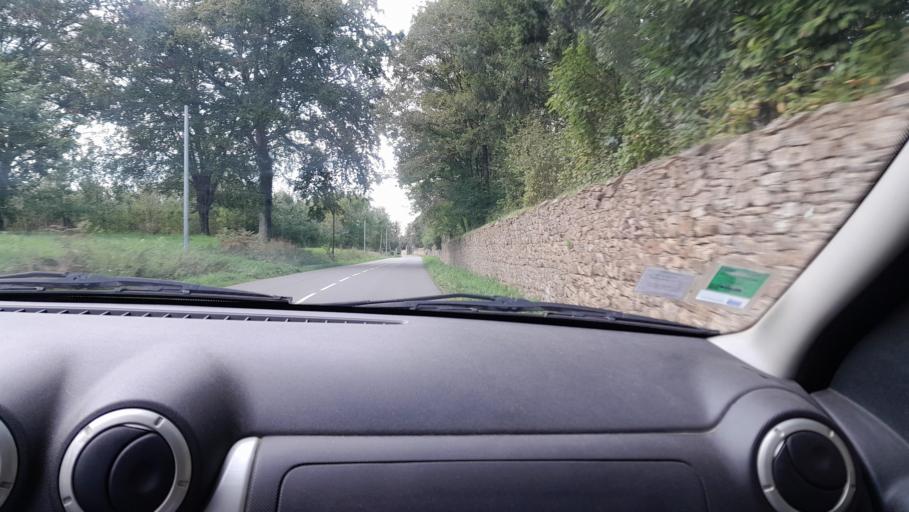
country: FR
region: Brittany
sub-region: Departement d'Ille-et-Vilaine
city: Le Pertre
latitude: 48.0364
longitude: -1.0414
